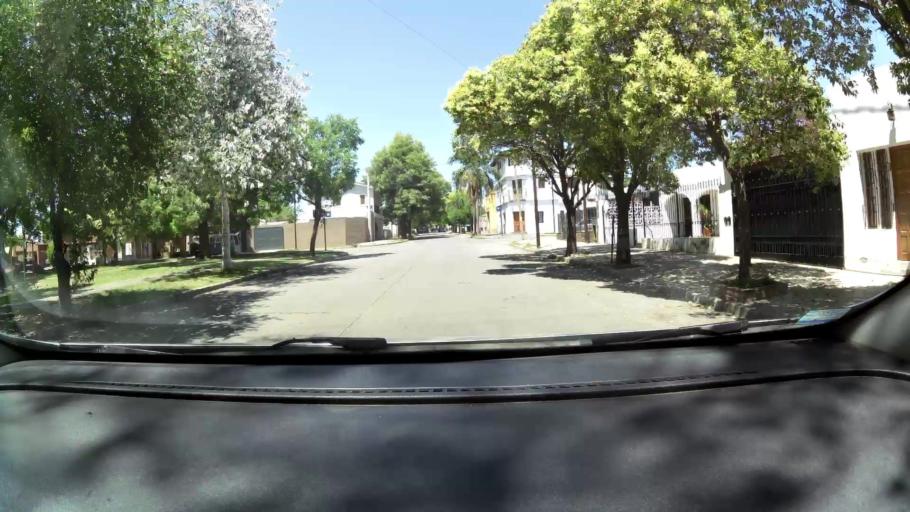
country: AR
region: Cordoba
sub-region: Departamento de Capital
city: Cordoba
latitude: -31.4128
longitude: -64.2137
